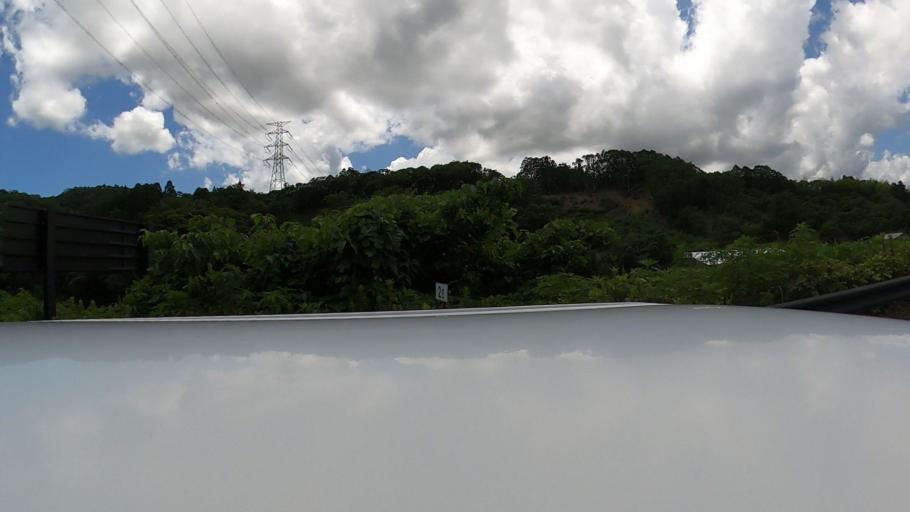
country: JP
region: Miyazaki
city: Nobeoka
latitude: 32.5806
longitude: 131.5193
